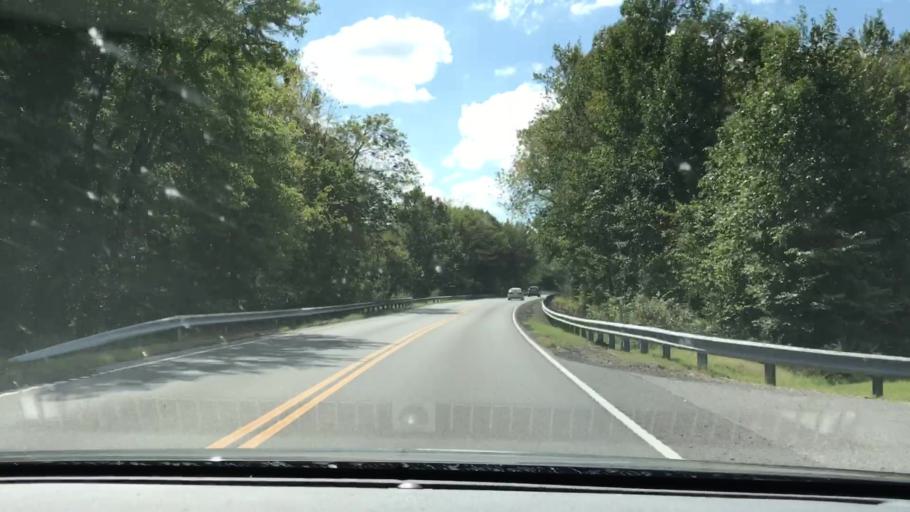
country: US
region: Kentucky
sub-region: McCracken County
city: Reidland
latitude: 36.9739
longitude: -88.5148
